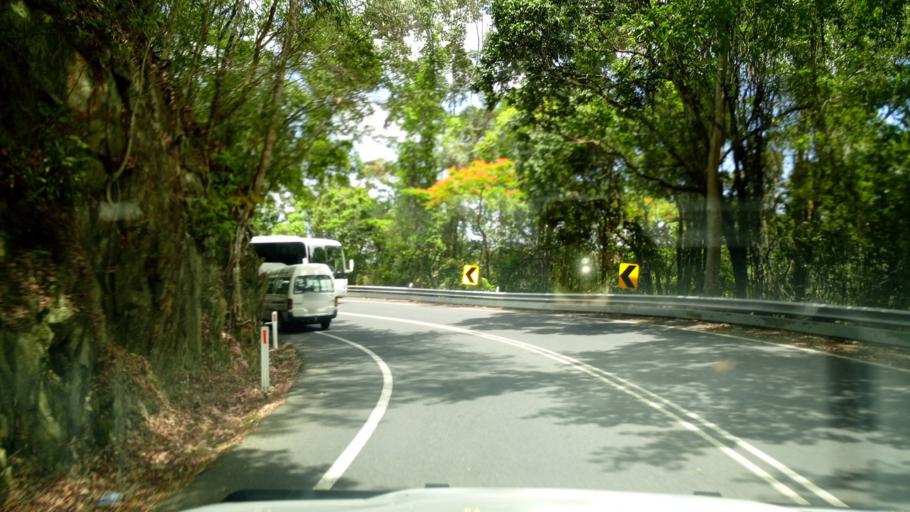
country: AU
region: Queensland
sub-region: Cairns
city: Redlynch
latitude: -16.8433
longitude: 145.6801
